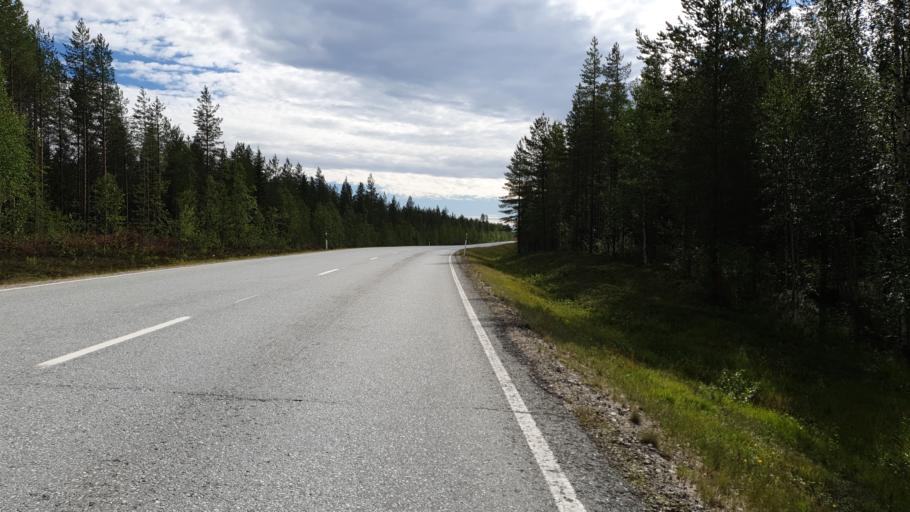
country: FI
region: Kainuu
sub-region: Kehys-Kainuu
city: Kuhmo
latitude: 64.4913
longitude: 29.8351
